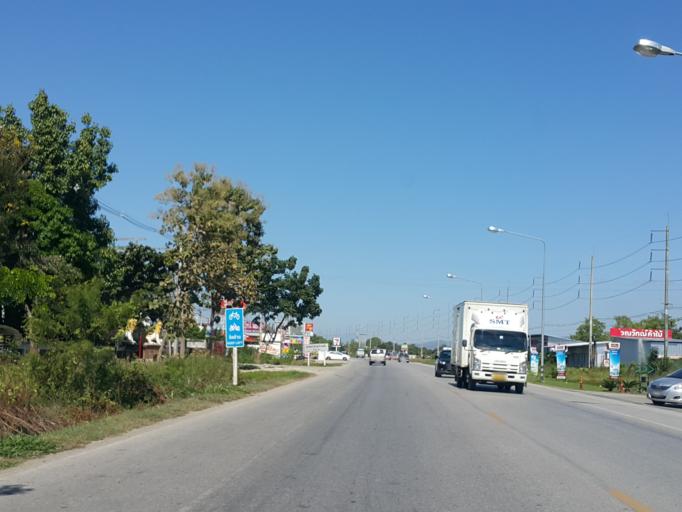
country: TH
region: Chiang Mai
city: San Sai
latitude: 18.7882
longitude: 99.0693
